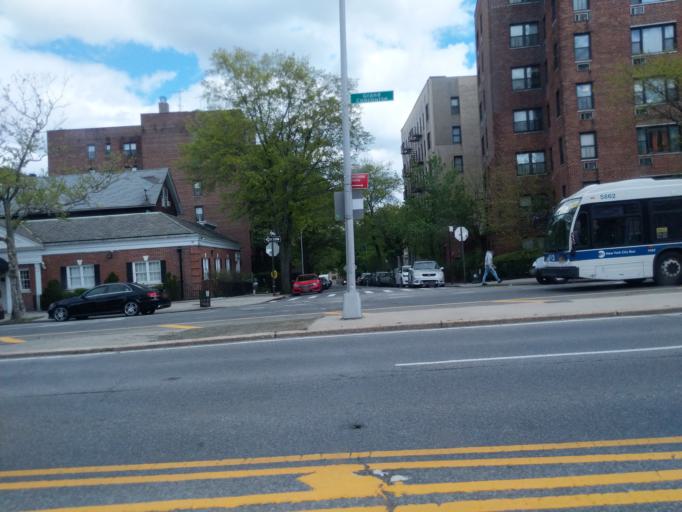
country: US
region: New York
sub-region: Bronx
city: The Bronx
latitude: 40.8727
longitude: -73.8874
